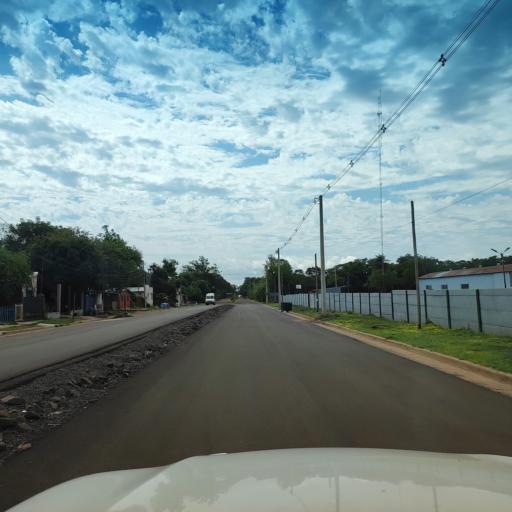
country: AR
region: Misiones
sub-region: Departamento de Capital
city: Posadas
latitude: -27.3591
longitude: -55.9269
